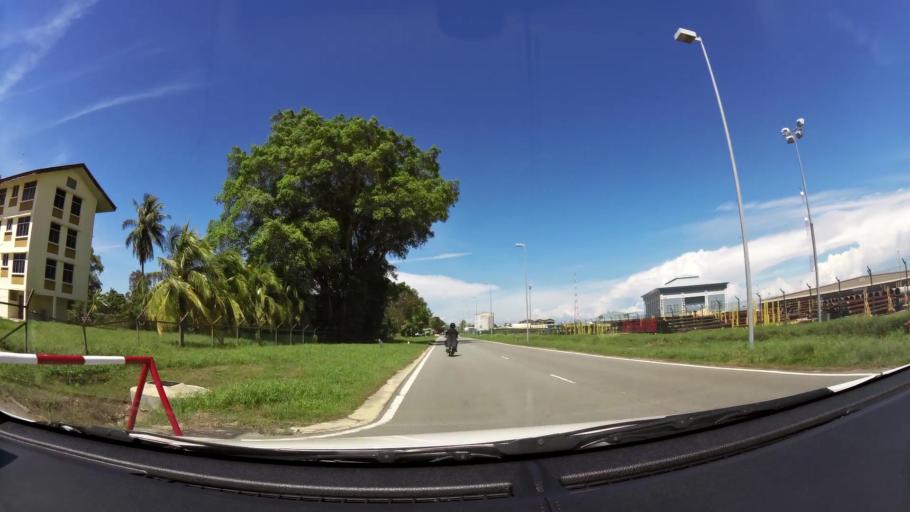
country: BN
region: Brunei and Muara
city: Bandar Seri Begawan
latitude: 5.0341
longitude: 115.0770
